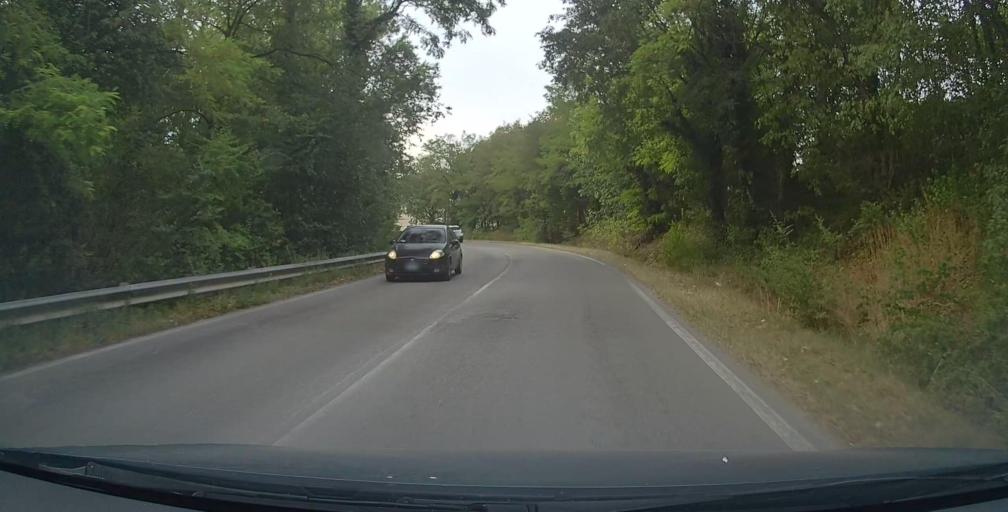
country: IT
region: Lombardy
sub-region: Provincia di Mantova
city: Monzambano
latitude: 45.3835
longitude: 10.6903
